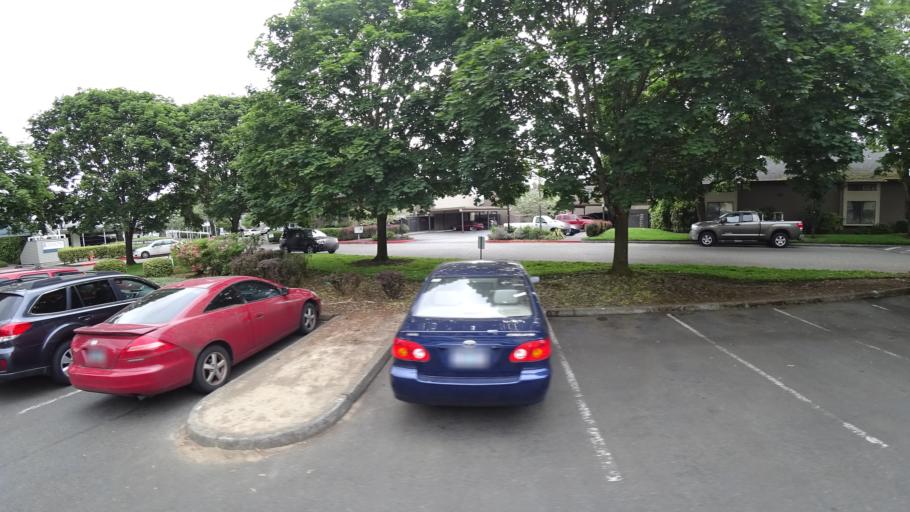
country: US
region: Washington
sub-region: Clark County
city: Vancouver
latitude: 45.6104
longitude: -122.6699
